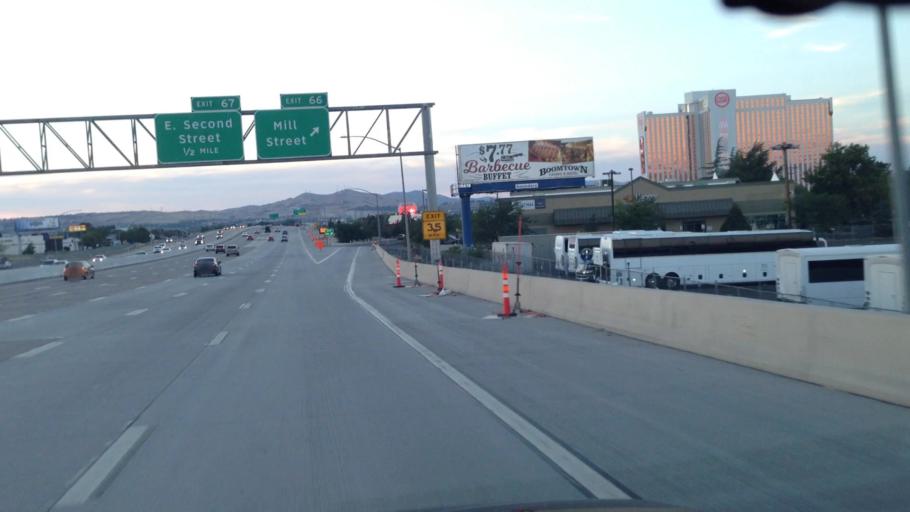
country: US
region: Nevada
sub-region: Washoe County
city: Sparks
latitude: 39.5145
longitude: -119.7815
